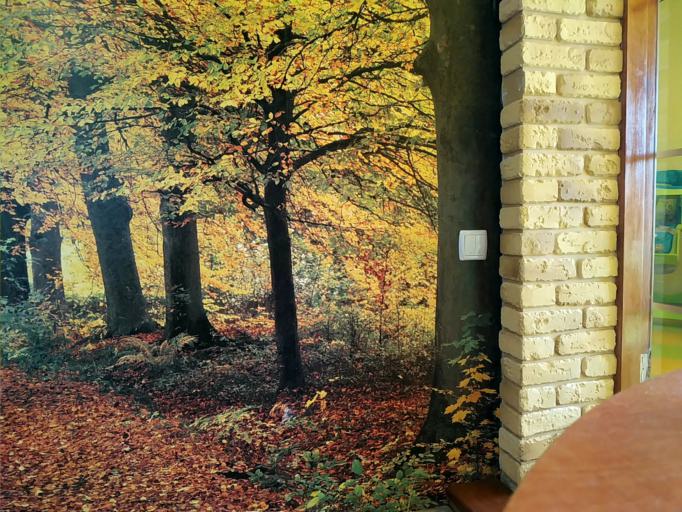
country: RU
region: Novgorod
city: Staraya Russa
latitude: 57.8353
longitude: 31.4740
